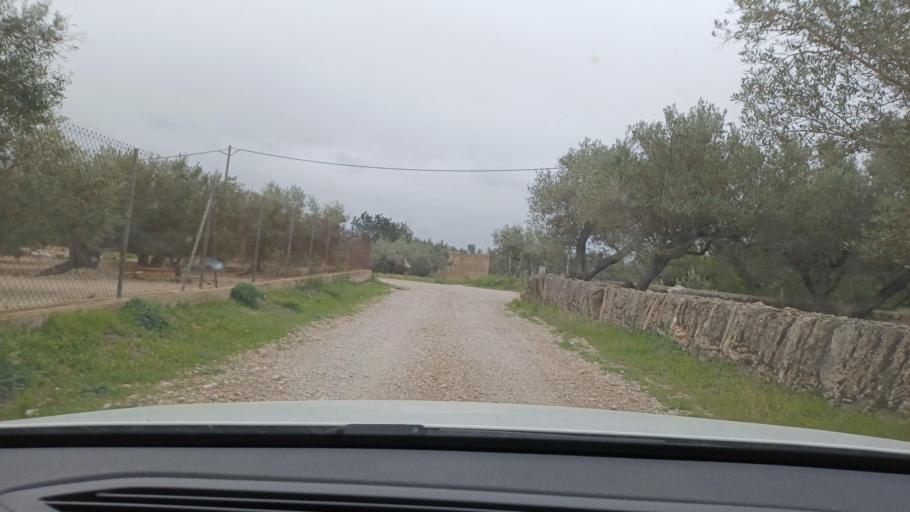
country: ES
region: Catalonia
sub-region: Provincia de Tarragona
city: Mas de Barberans
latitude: 40.8052
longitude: 0.4102
